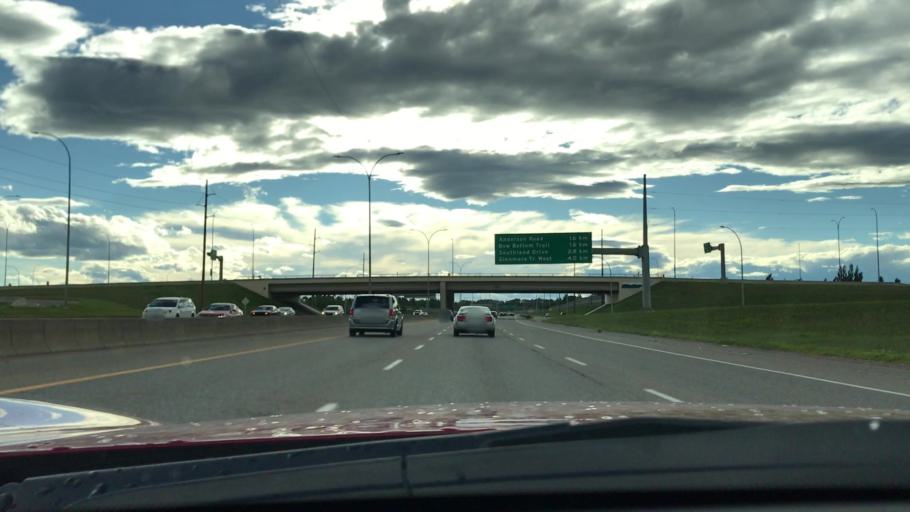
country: CA
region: Alberta
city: Calgary
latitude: 50.9483
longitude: -114.0014
